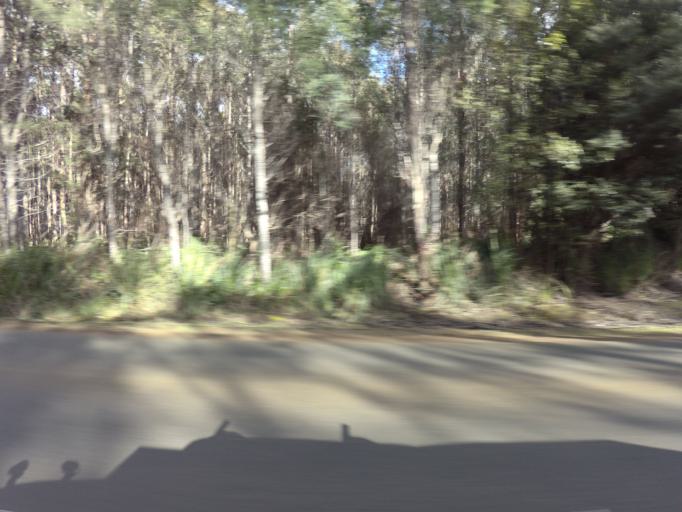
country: AU
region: Tasmania
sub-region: Huon Valley
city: Geeveston
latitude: -43.3477
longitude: 146.9616
